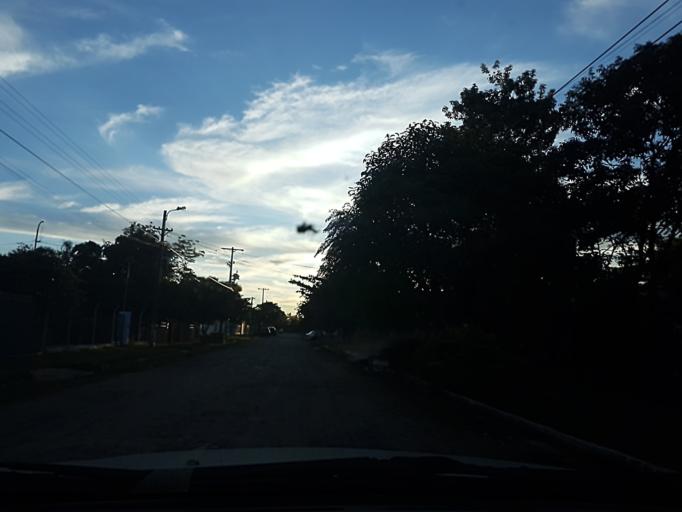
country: PY
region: Central
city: Colonia Mariano Roque Alonso
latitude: -25.2081
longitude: -57.5363
